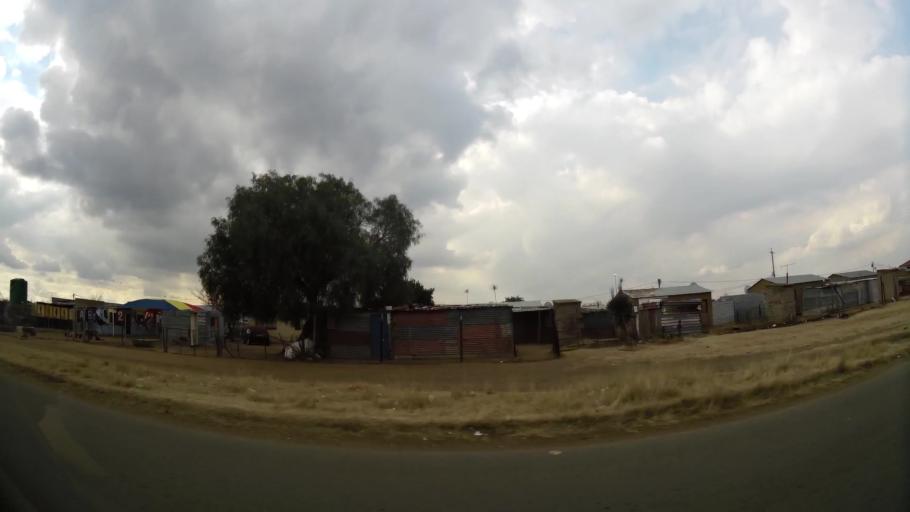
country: ZA
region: Orange Free State
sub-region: Fezile Dabi District Municipality
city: Sasolburg
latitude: -26.8544
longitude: 27.8746
